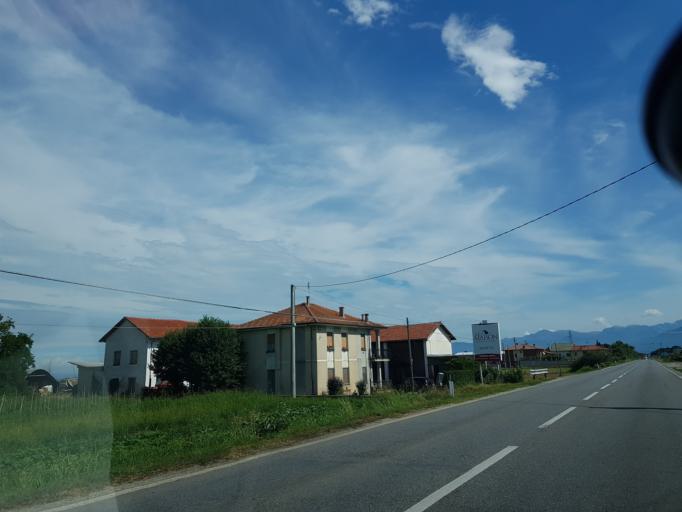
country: IT
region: Piedmont
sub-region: Provincia di Cuneo
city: Busca
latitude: 44.4936
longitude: 7.4961
